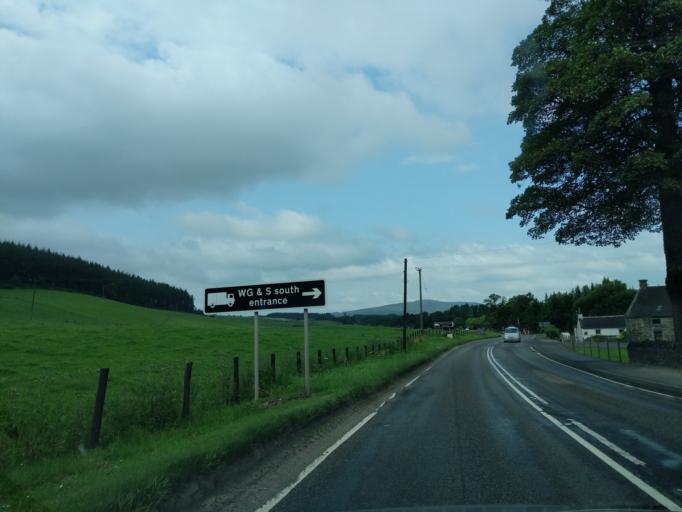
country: GB
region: Scotland
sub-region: Moray
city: Dufftown
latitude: 57.4564
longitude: -3.1315
